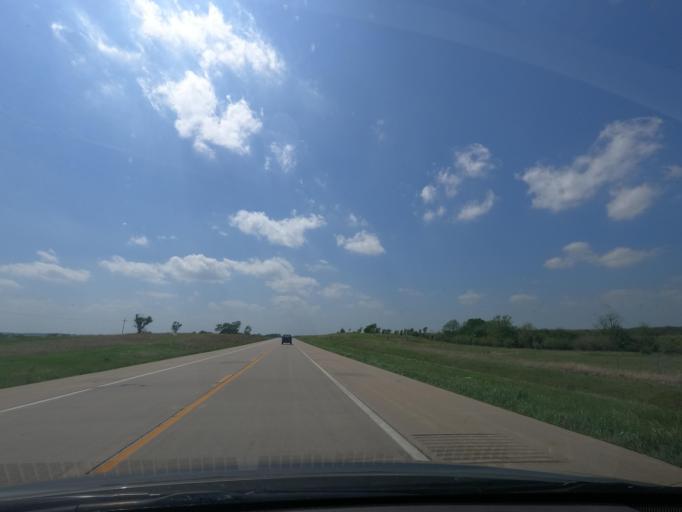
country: US
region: Kansas
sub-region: Elk County
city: Howard
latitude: 37.6278
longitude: -96.1036
